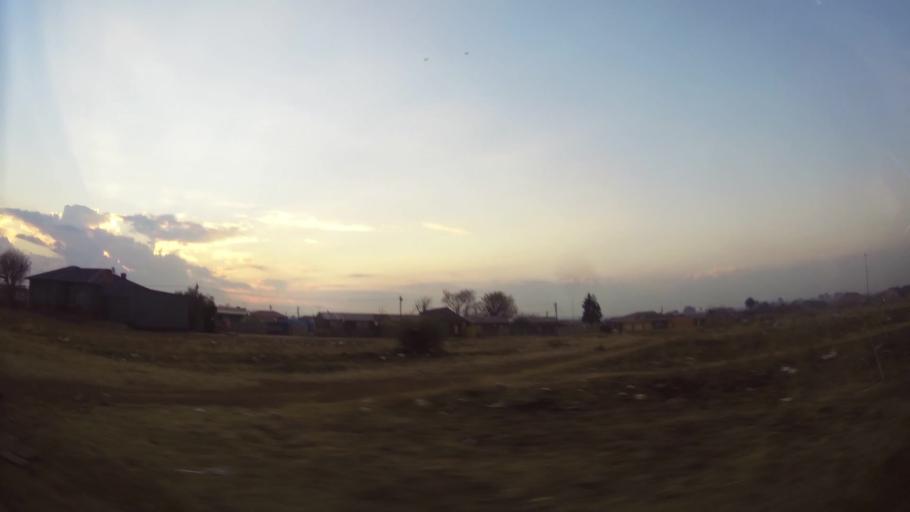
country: ZA
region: Gauteng
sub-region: City of Johannesburg Metropolitan Municipality
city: Orange Farm
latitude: -26.5513
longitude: 27.8819
